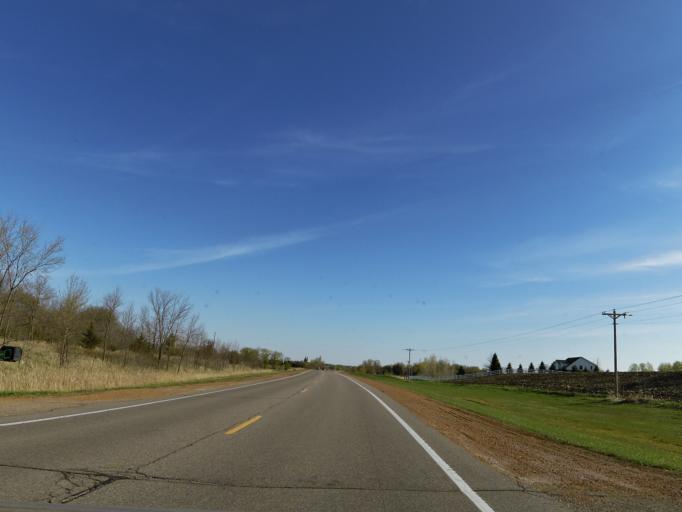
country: US
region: Minnesota
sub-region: Scott County
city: Prior Lake
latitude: 44.6593
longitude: -93.5006
